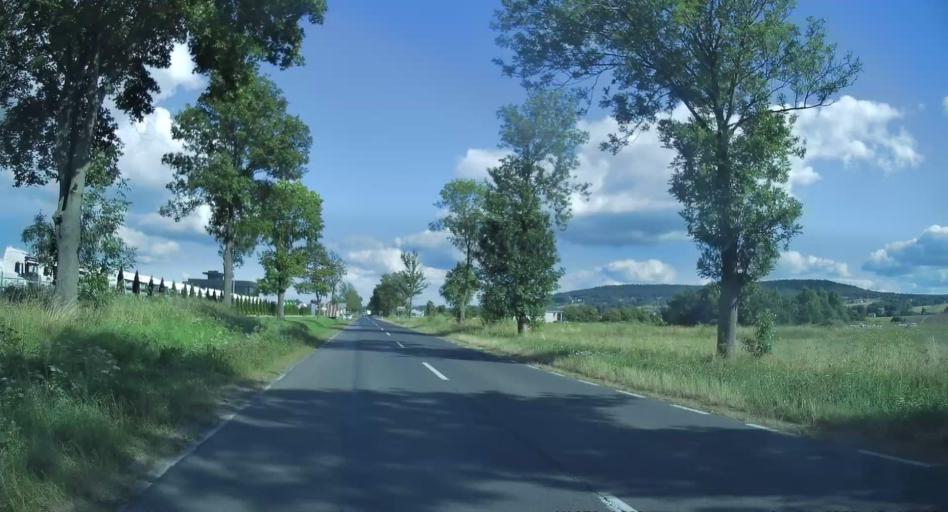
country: PL
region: Swietokrzyskie
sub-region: Powiat kielecki
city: Bodzentyn
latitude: 50.9516
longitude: 20.9253
